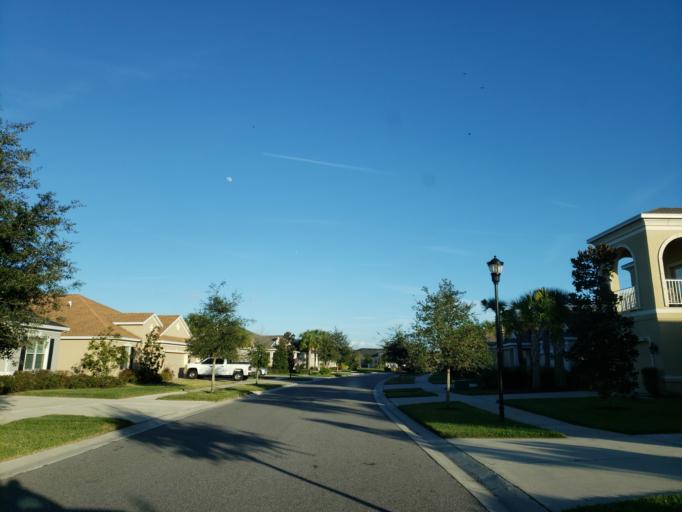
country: US
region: Florida
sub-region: Hillsborough County
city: Fish Hawk
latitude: 27.8385
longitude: -82.2045
